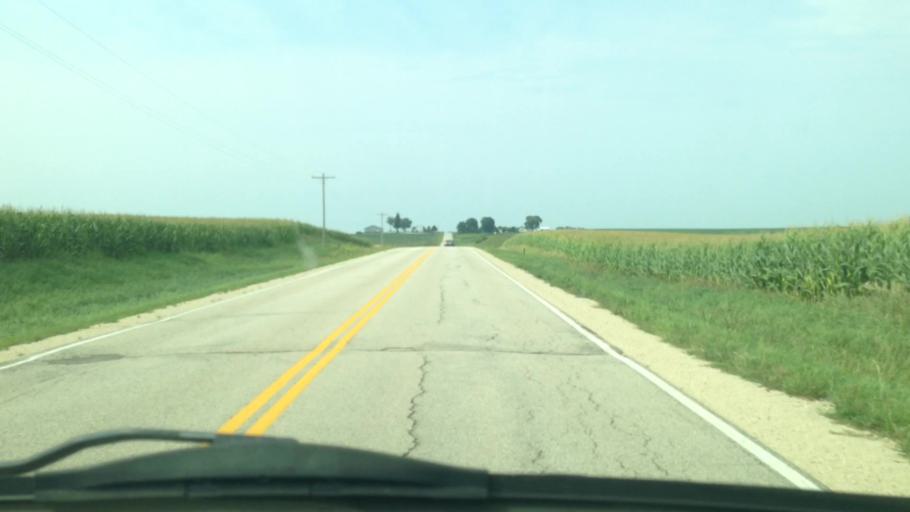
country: US
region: Minnesota
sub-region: Winona County
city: Lewiston
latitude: 43.8837
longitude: -91.9595
